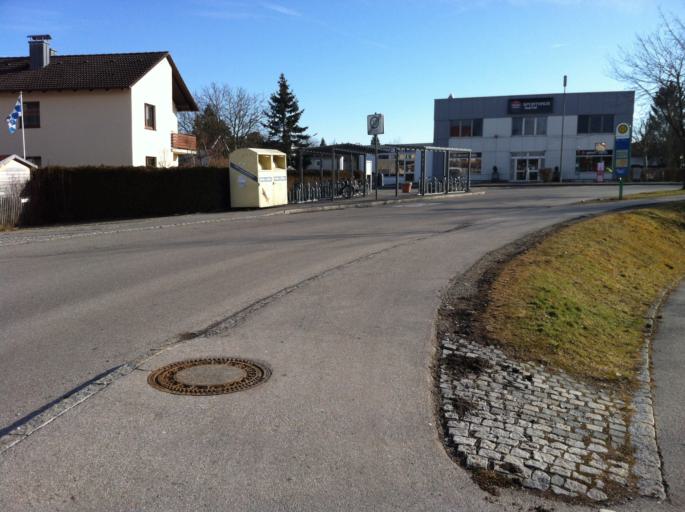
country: DE
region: Bavaria
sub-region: Upper Bavaria
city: Wolfratshausen
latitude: 47.9001
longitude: 11.4388
